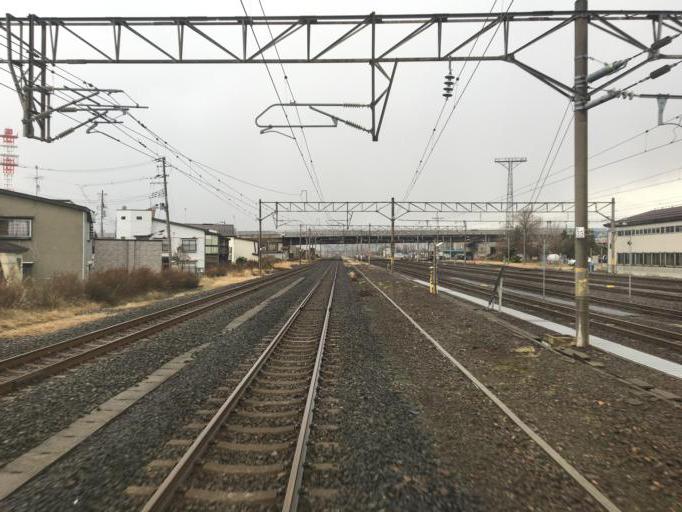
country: JP
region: Aomori
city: Aomori Shi
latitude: 40.8178
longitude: 140.7414
